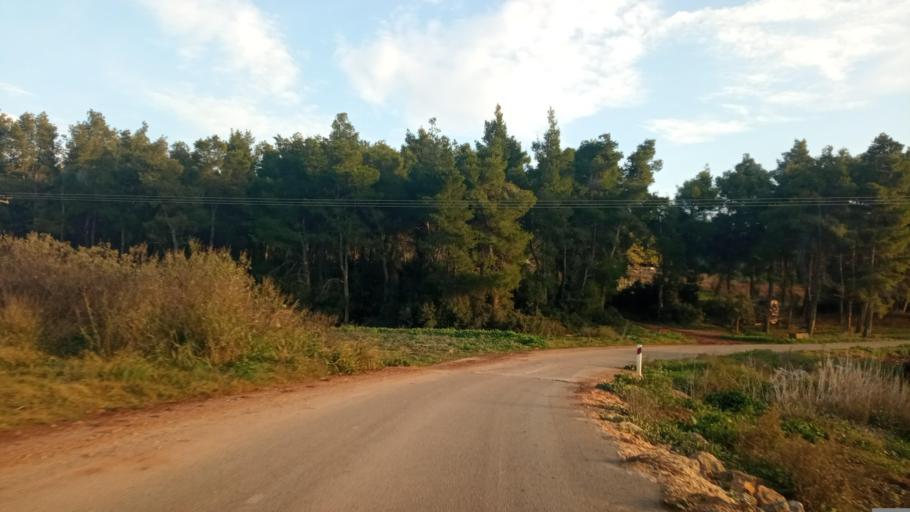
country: GR
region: Central Greece
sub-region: Nomos Evvoias
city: Kastella
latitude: 38.5651
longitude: 23.7099
